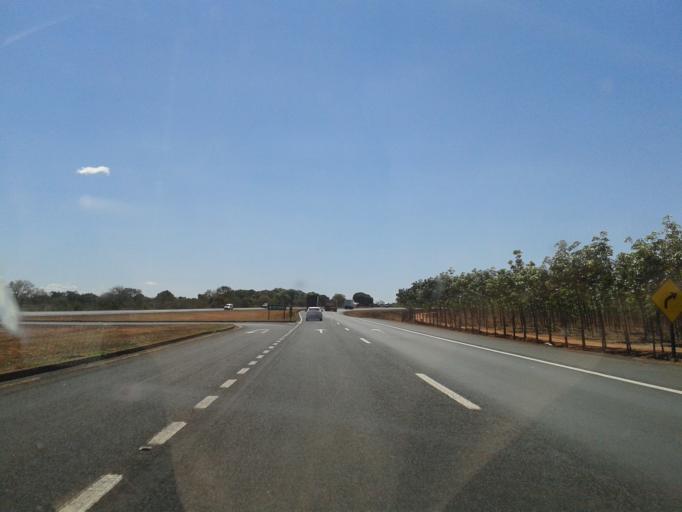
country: BR
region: Minas Gerais
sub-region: Monte Alegre De Minas
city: Monte Alegre de Minas
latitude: -18.8164
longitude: -49.0870
